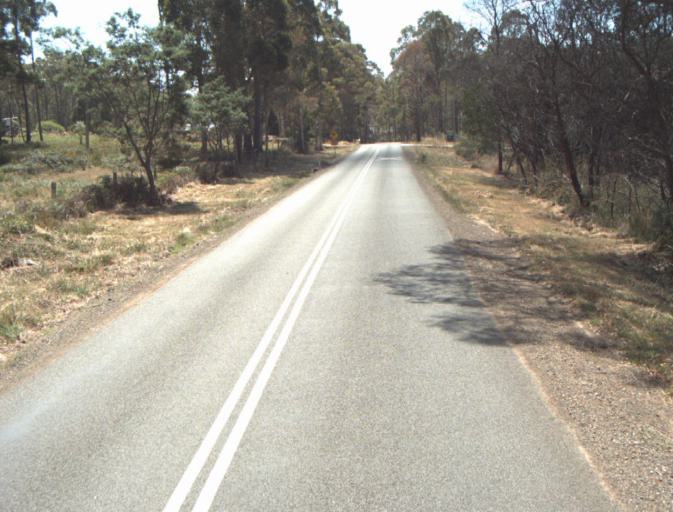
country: AU
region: Tasmania
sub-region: Launceston
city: Mayfield
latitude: -41.2810
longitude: 147.1262
